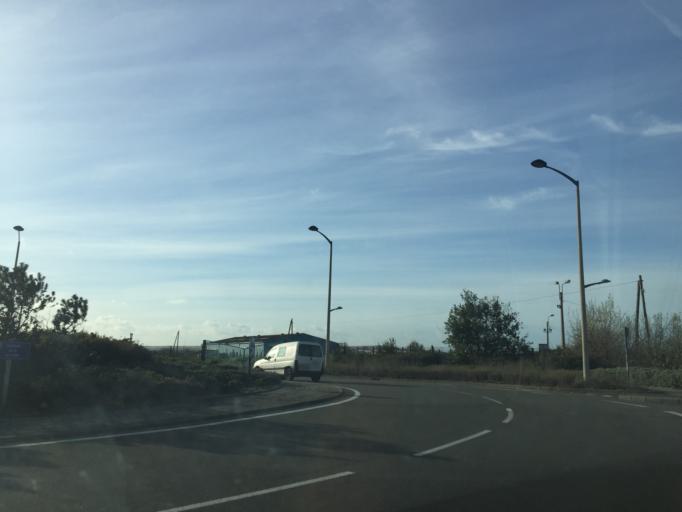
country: FR
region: Nord-Pas-de-Calais
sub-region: Departement du Pas-de-Calais
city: Calais
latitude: 50.9573
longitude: 1.8346
